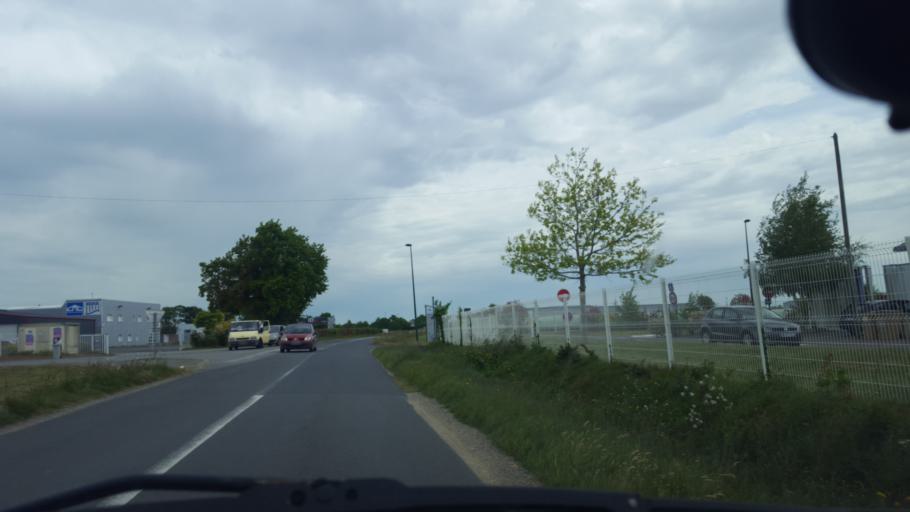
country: FR
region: Pays de la Loire
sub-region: Departement de la Loire-Atlantique
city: Machecoul
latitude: 46.9782
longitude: -1.8022
